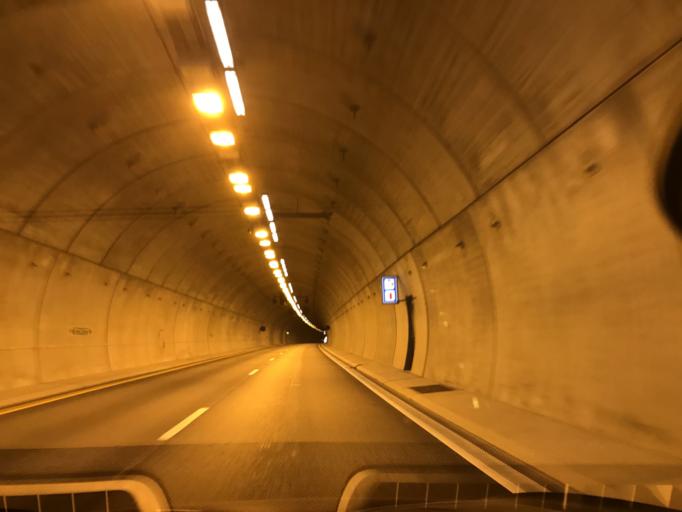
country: NO
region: Akershus
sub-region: Eidsvoll
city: Eidsvoll
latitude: 60.4336
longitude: 11.2409
